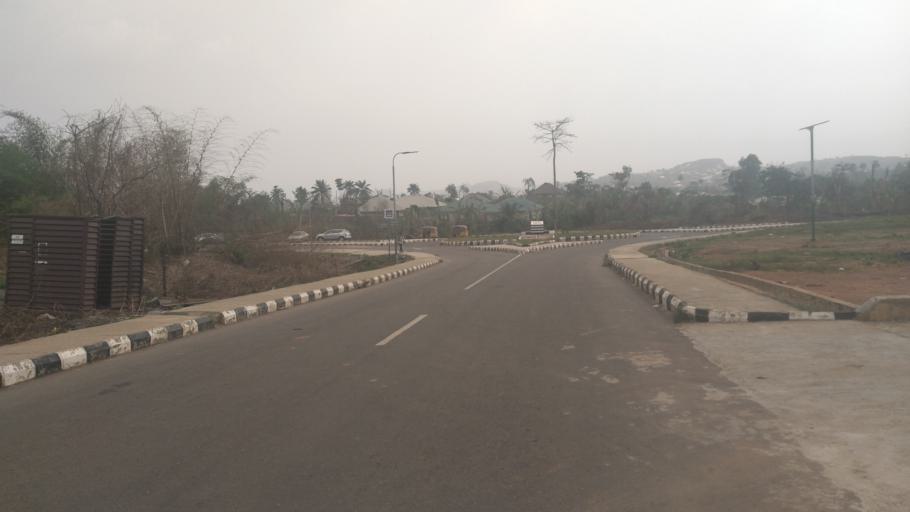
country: NG
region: Ondo
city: Ilare
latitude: 7.2956
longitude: 5.1355
